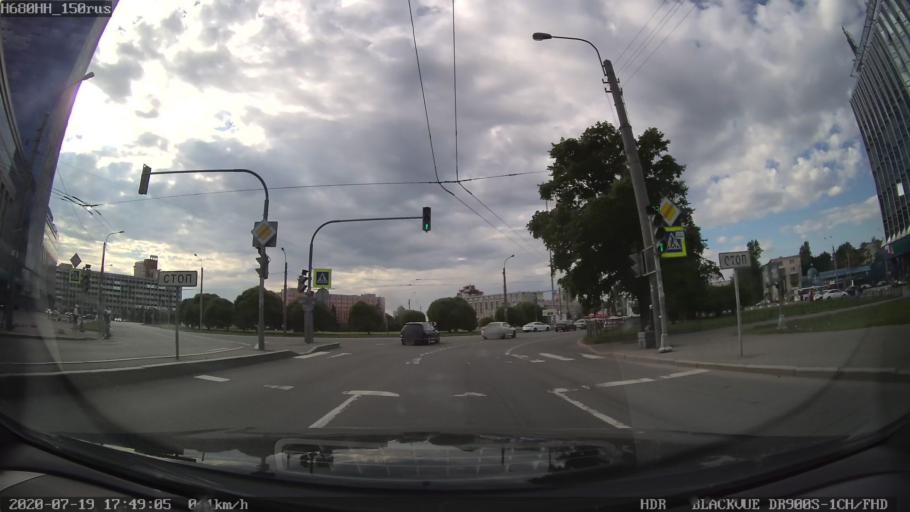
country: RU
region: St.-Petersburg
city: Avtovo
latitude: 59.8509
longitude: 30.3071
